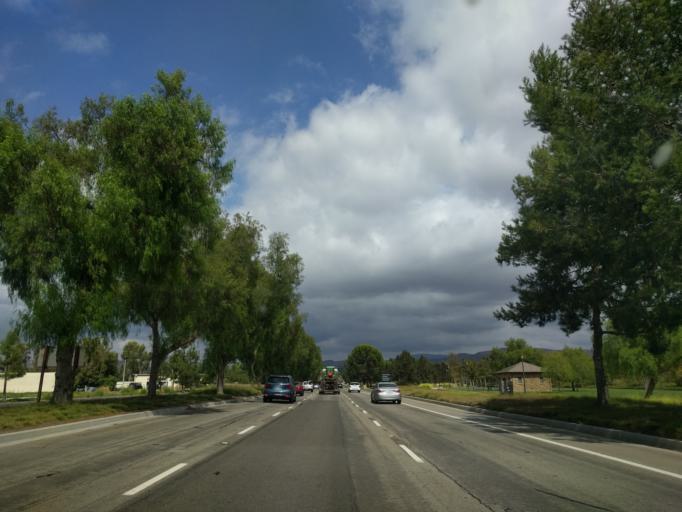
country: US
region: California
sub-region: Orange County
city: North Tustin
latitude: 33.7033
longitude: -117.7551
